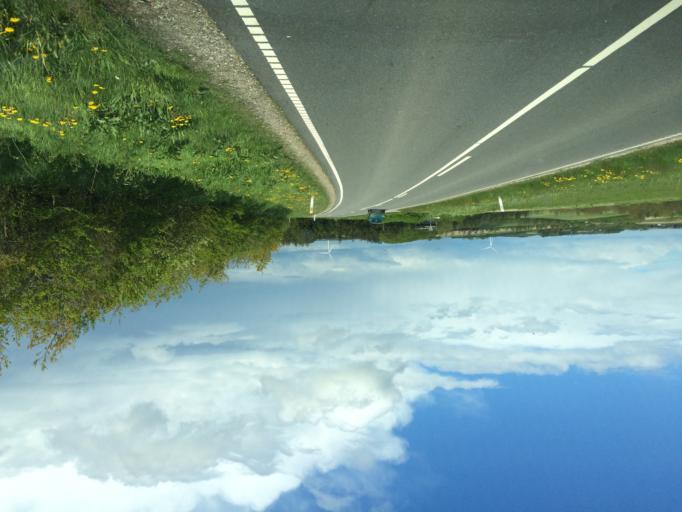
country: DK
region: North Denmark
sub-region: Vesthimmerland Kommune
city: Farso
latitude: 56.8162
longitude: 9.3587
